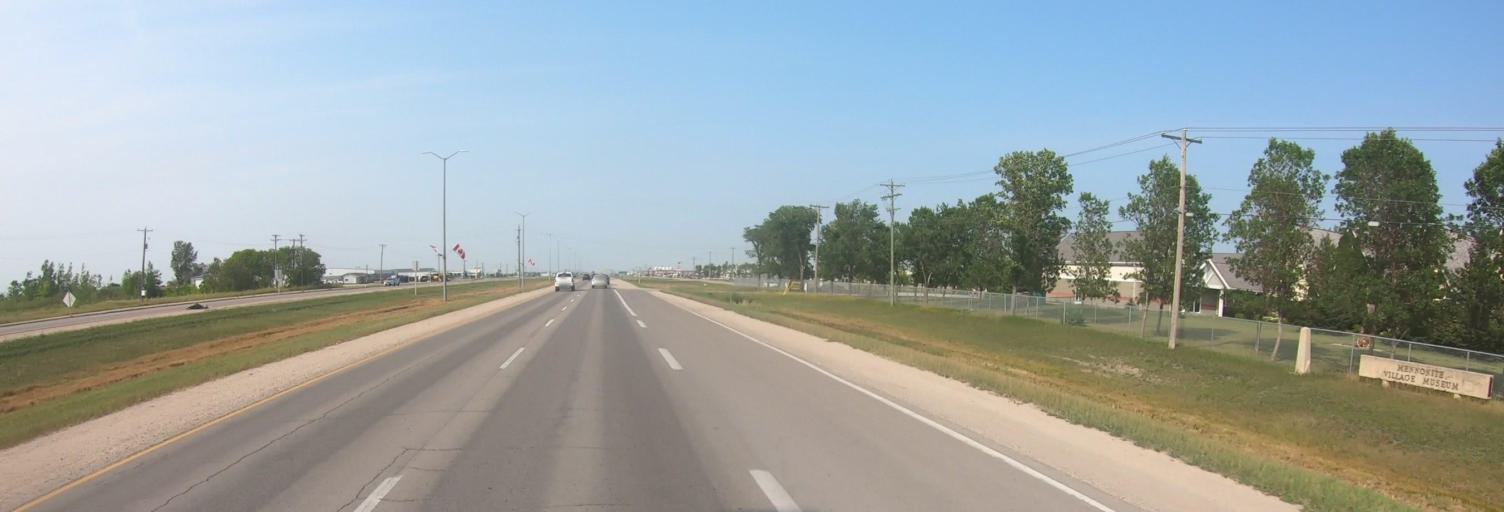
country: CA
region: Manitoba
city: Steinbach
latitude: 49.5510
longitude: -96.6881
